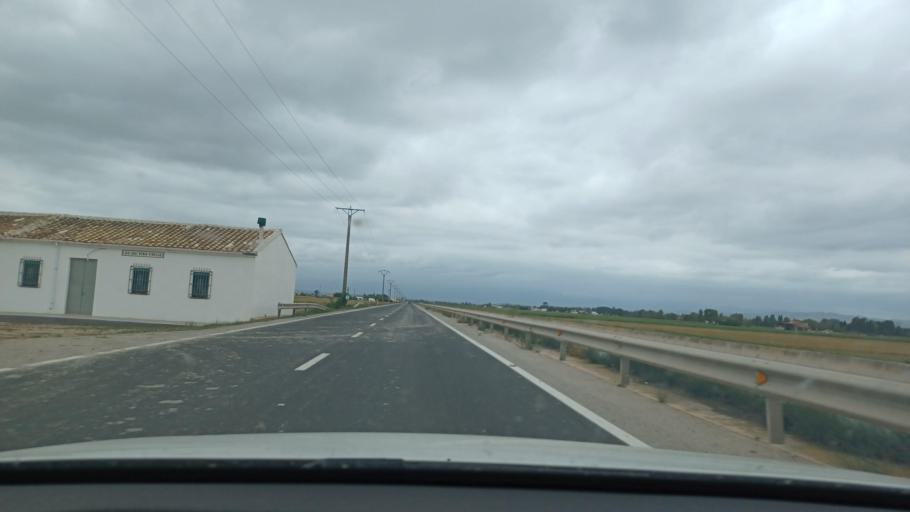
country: ES
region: Catalonia
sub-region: Provincia de Tarragona
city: Deltebre
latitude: 40.7074
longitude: 0.6973
